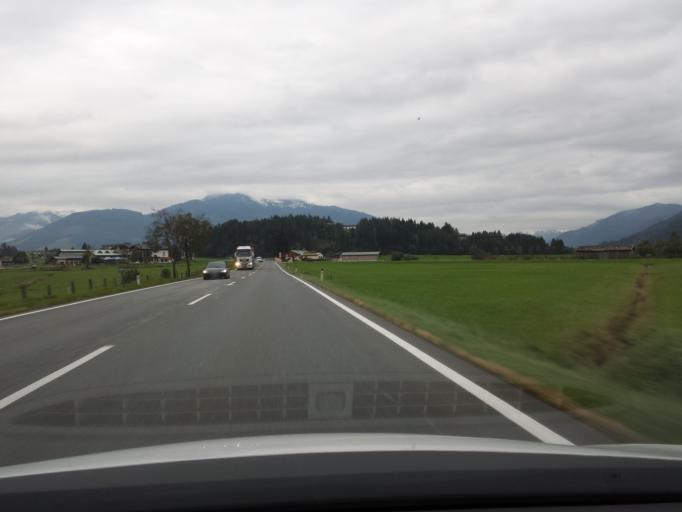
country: AT
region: Salzburg
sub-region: Politischer Bezirk Zell am See
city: Saalfelden am Steinernen Meer
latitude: 47.4586
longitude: 12.8294
